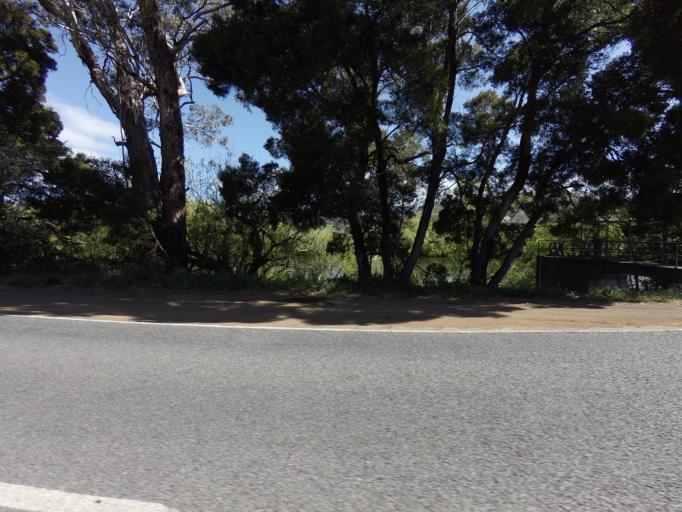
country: AU
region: Tasmania
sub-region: Derwent Valley
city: New Norfolk
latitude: -42.7675
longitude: 147.0253
